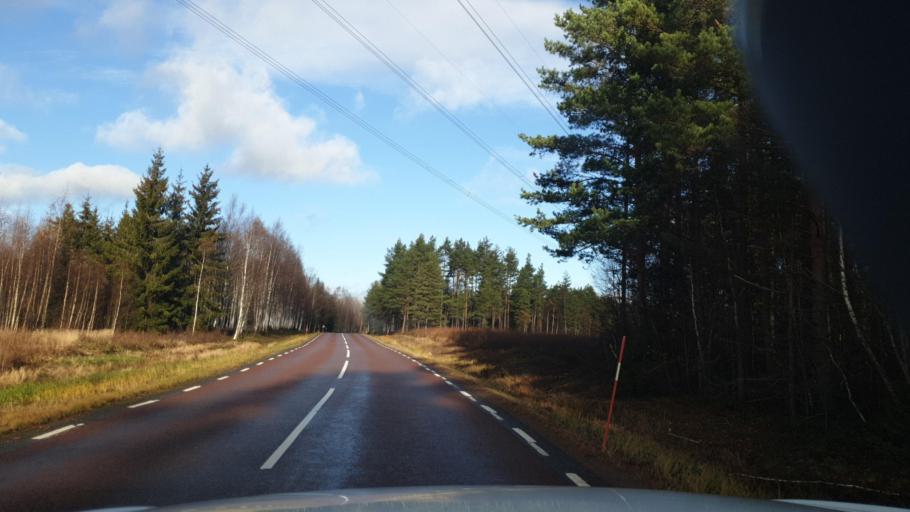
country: SE
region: Vaermland
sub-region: Grums Kommun
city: Grums
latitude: 59.4364
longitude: 12.9796
